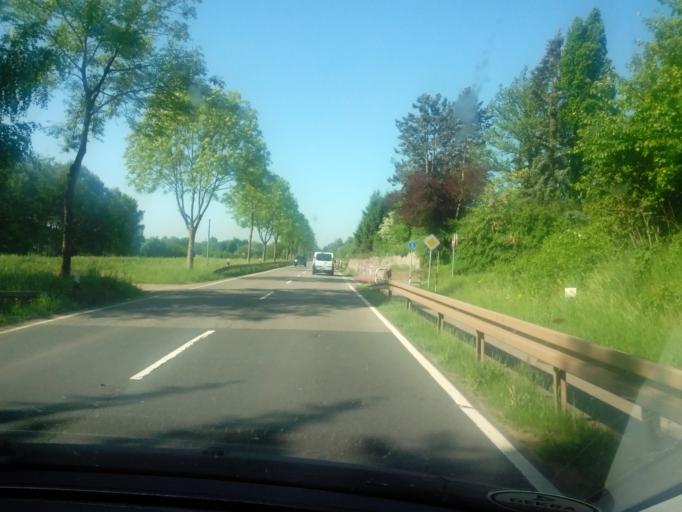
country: DE
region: Saarland
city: Nalbach
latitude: 49.3849
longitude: 6.8022
